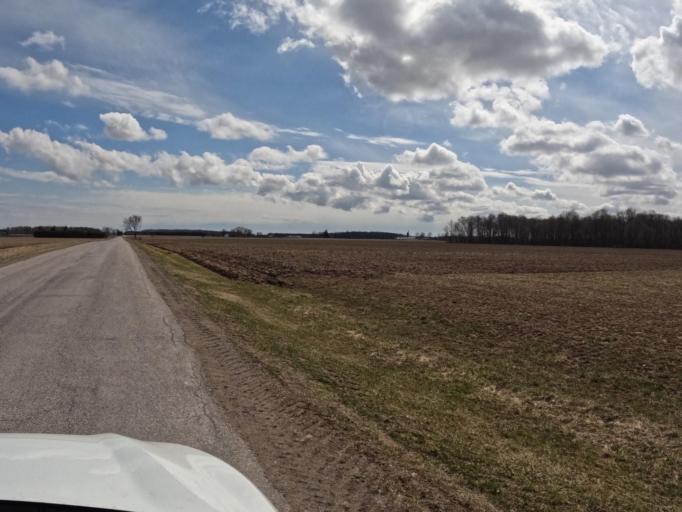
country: CA
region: Ontario
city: Norfolk County
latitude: 42.9233
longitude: -80.1984
